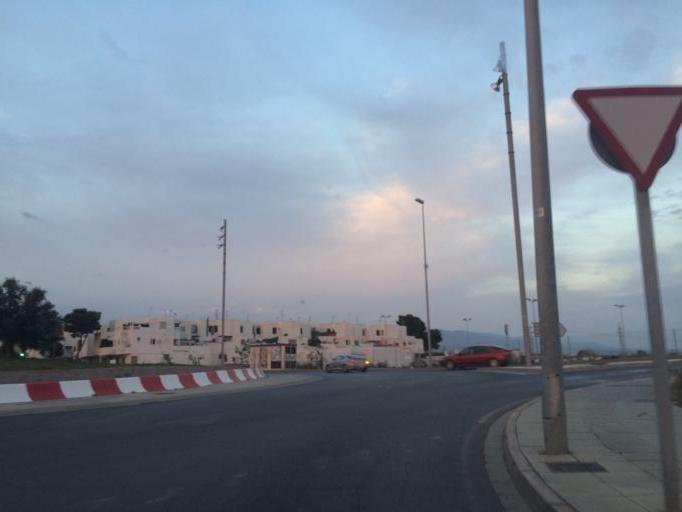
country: ES
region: Andalusia
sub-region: Provincia de Almeria
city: Almeria
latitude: 36.8430
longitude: -2.4322
